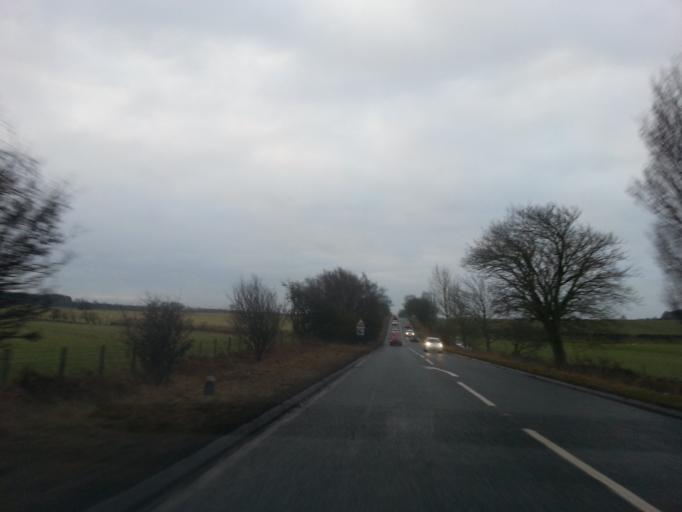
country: GB
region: England
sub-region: County Durham
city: Hamsterley
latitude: 54.6989
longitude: -1.7841
